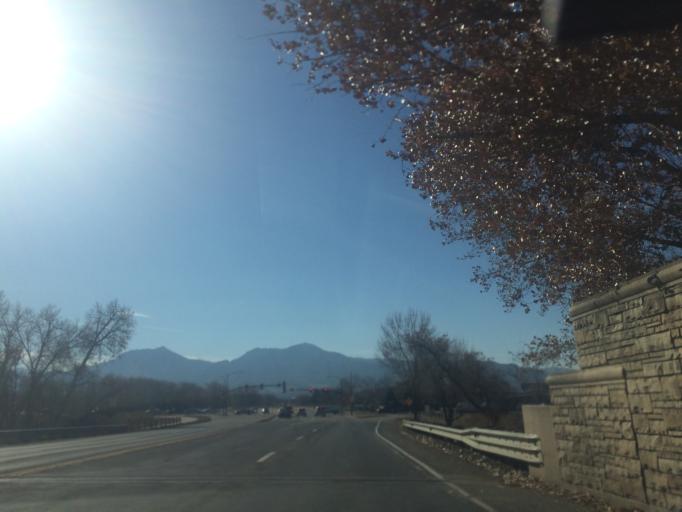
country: US
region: Colorado
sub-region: Boulder County
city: Boulder
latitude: 40.0285
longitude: -105.2237
